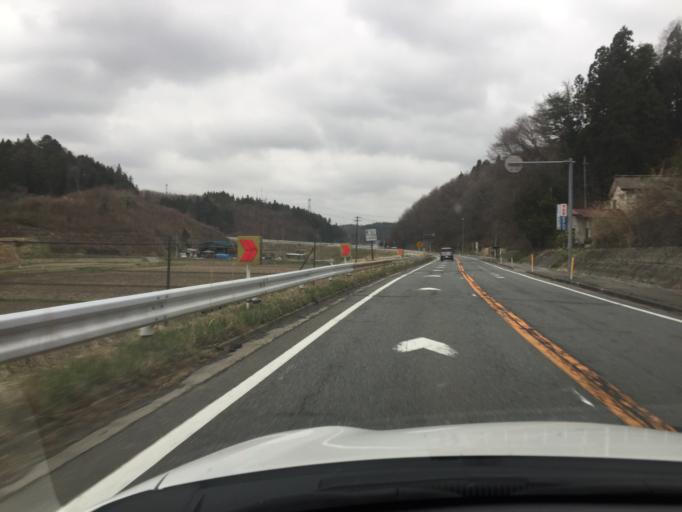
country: JP
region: Fukushima
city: Ishikawa
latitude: 37.1889
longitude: 140.6431
